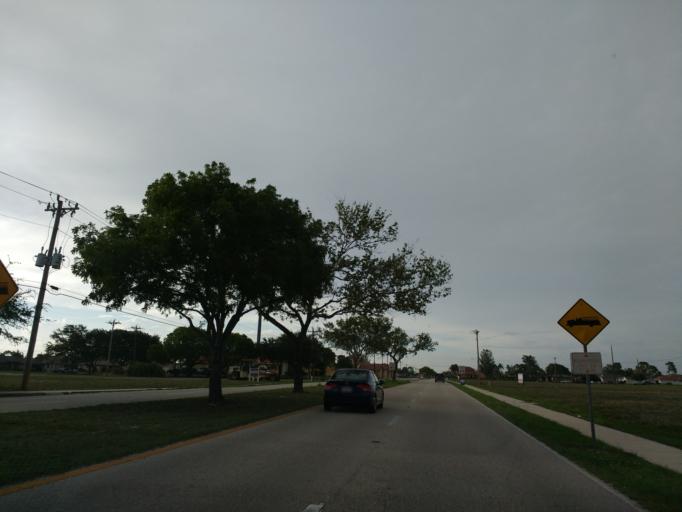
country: US
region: Florida
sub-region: Lee County
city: Cape Coral
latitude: 26.5650
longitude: -82.0066
